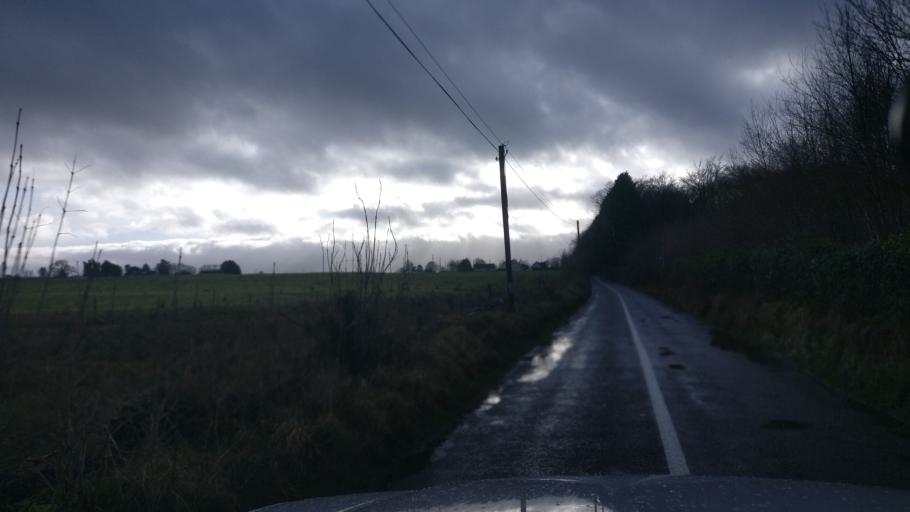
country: IE
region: Connaught
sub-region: County Galway
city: Loughrea
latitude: 53.2396
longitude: -8.6211
